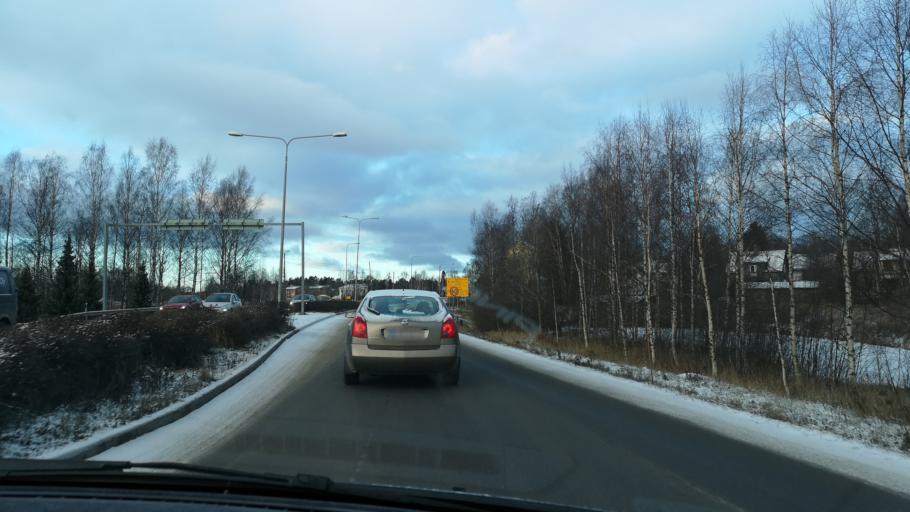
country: FI
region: Ostrobothnia
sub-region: Vaasa
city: Vaasa
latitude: 63.1112
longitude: 21.6196
